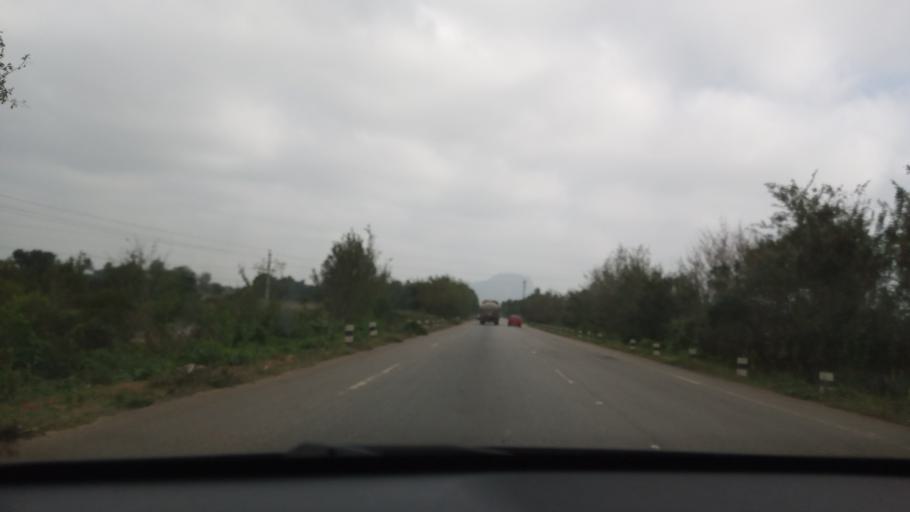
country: IN
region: Karnataka
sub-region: Chikkaballapur
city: Chintamani
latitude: 13.3097
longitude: 77.9766
